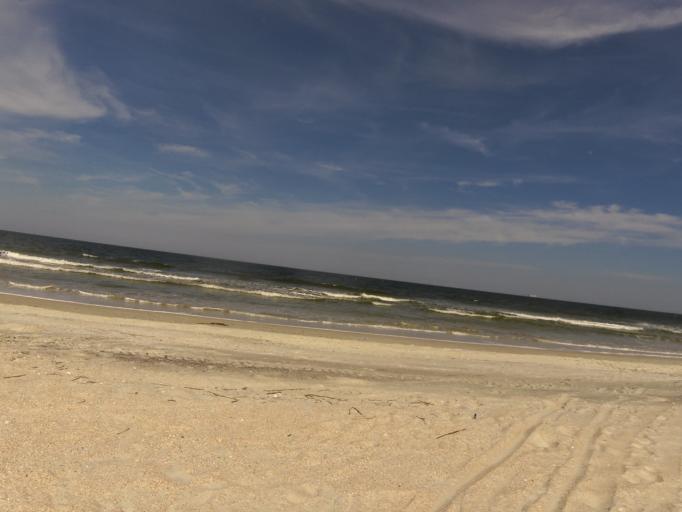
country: US
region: Florida
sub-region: Duval County
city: Atlantic Beach
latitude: 30.4560
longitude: -81.4109
